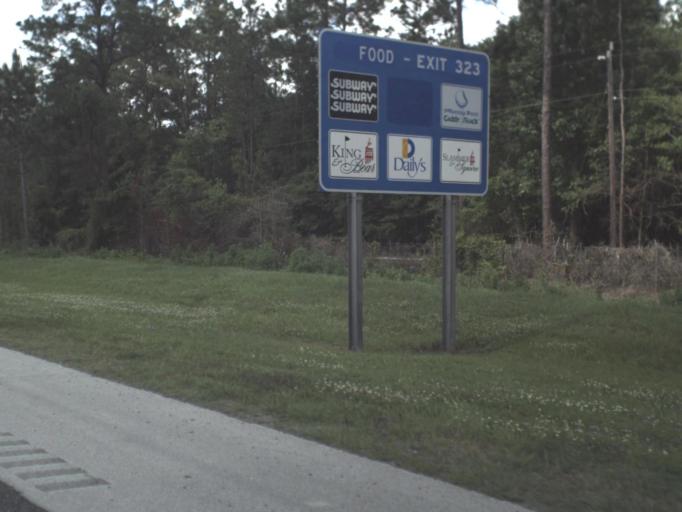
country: US
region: Florida
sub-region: Saint Johns County
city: Villano Beach
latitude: 29.9732
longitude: -81.4538
